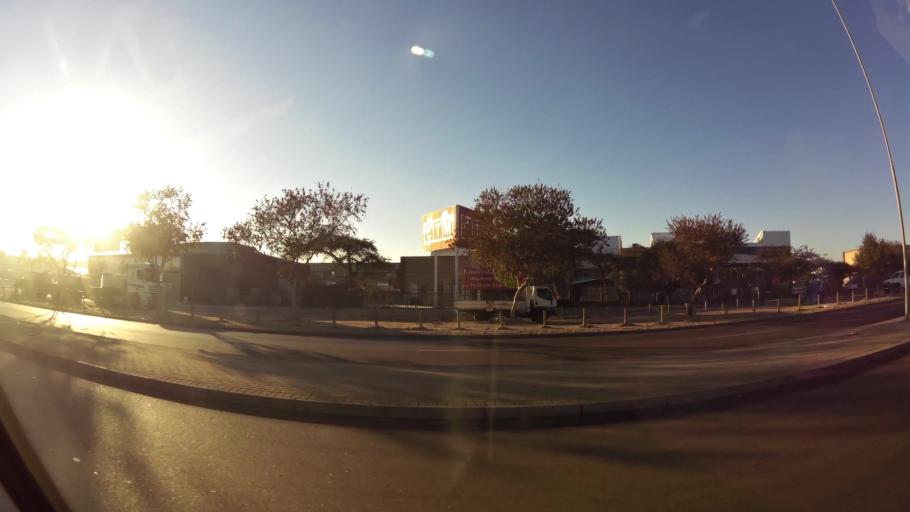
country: ZA
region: Limpopo
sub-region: Capricorn District Municipality
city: Polokwane
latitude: -23.9104
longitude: 29.4402
